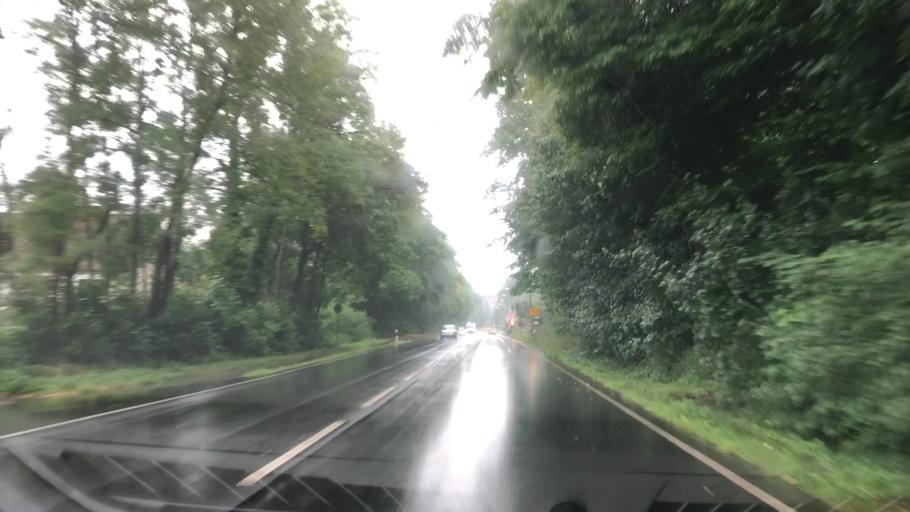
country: DE
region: Lower Saxony
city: Buckeburg
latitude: 52.2596
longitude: 9.0340
